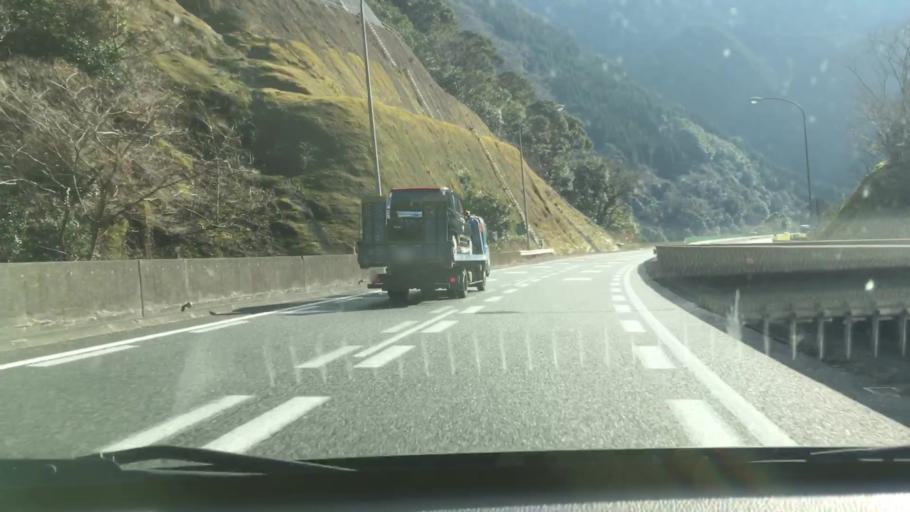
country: JP
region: Kumamoto
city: Hitoyoshi
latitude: 32.3240
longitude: 130.7583
